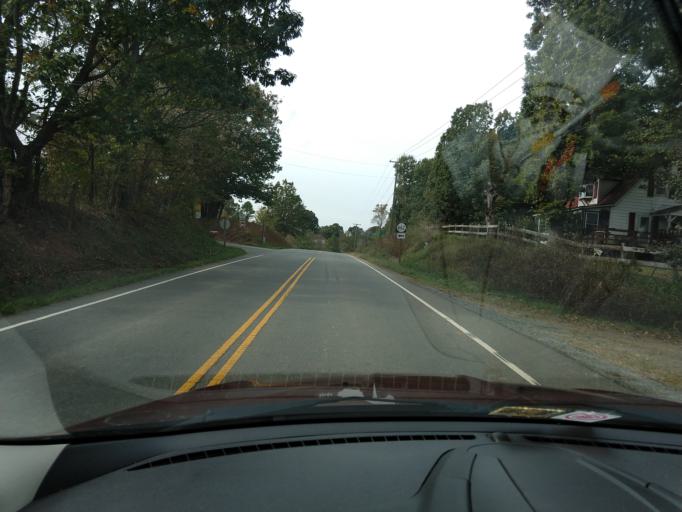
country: US
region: Virginia
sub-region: Franklin County
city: Union Hall
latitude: 36.9942
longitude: -79.7076
